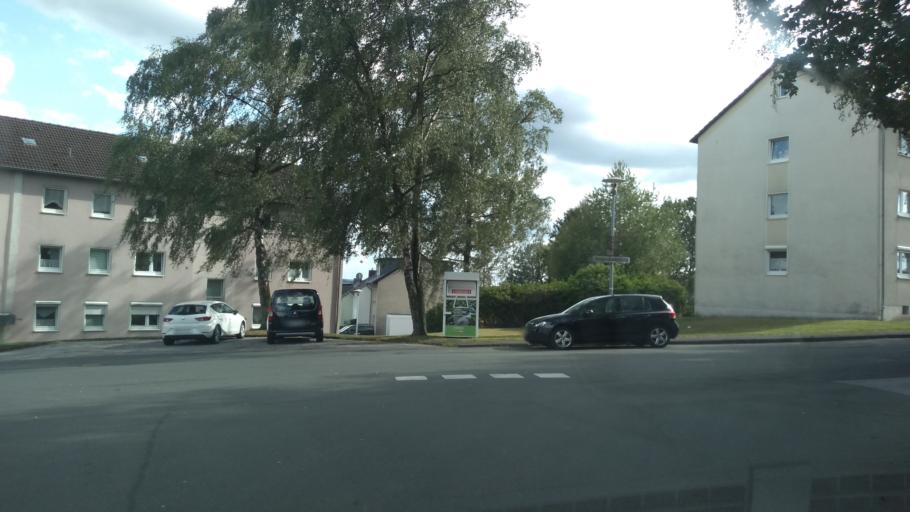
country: DE
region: North Rhine-Westphalia
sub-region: Regierungsbezirk Arnsberg
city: Luedenscheid
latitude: 51.2251
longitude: 7.5971
